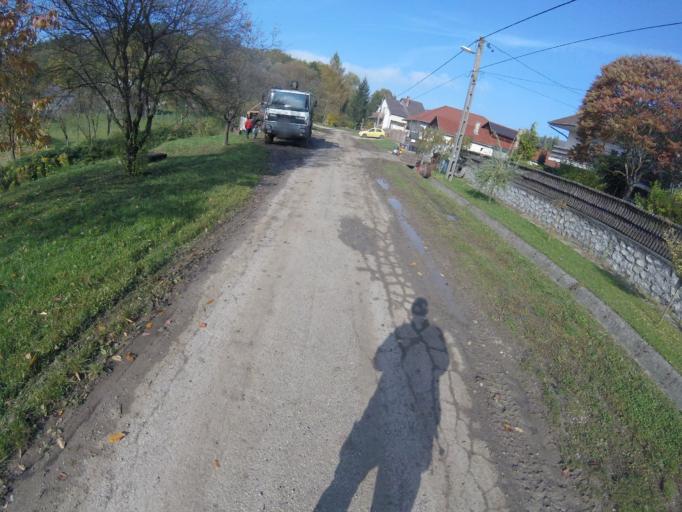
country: HU
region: Borsod-Abauj-Zemplen
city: Putnok
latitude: 48.2179
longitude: 20.4398
